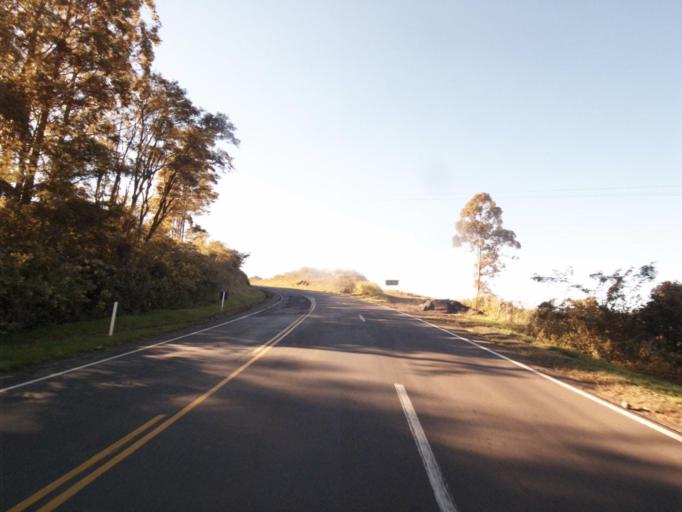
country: AR
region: Misiones
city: Bernardo de Irigoyen
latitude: -26.3304
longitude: -53.5444
